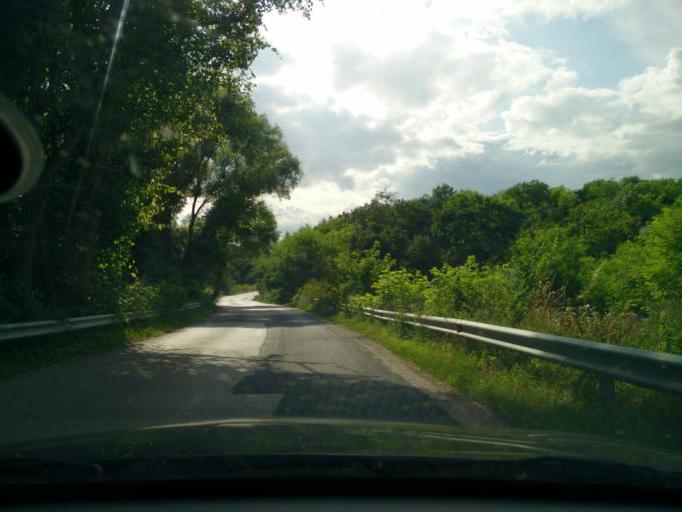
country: HU
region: Komarom-Esztergom
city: Baj
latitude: 47.6672
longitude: 18.3950
